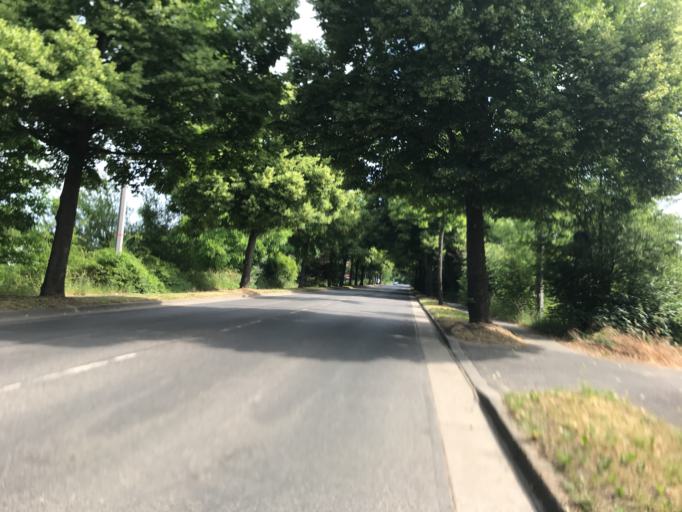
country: DE
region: Hesse
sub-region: Regierungsbezirk Darmstadt
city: Wiesbaden
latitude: 50.0535
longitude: 8.2073
